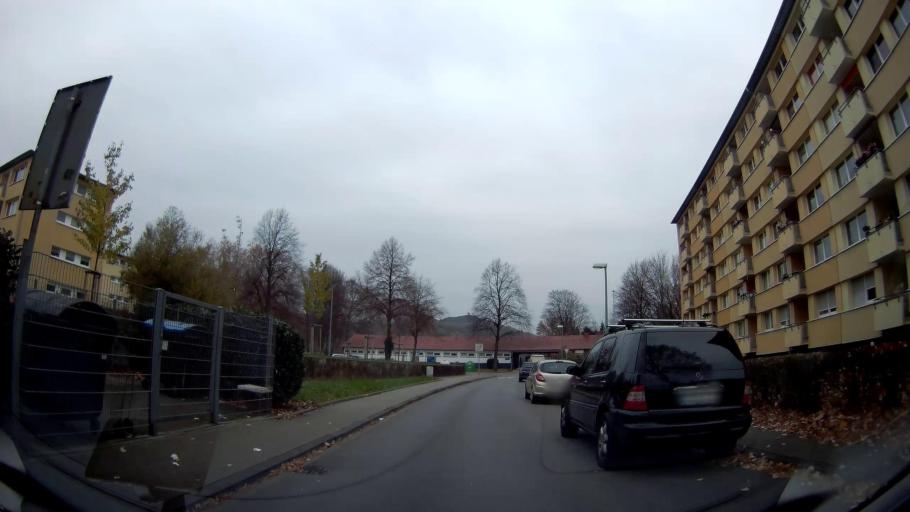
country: DE
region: North Rhine-Westphalia
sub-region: Regierungsbezirk Munster
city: Gladbeck
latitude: 51.5556
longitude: 7.0424
